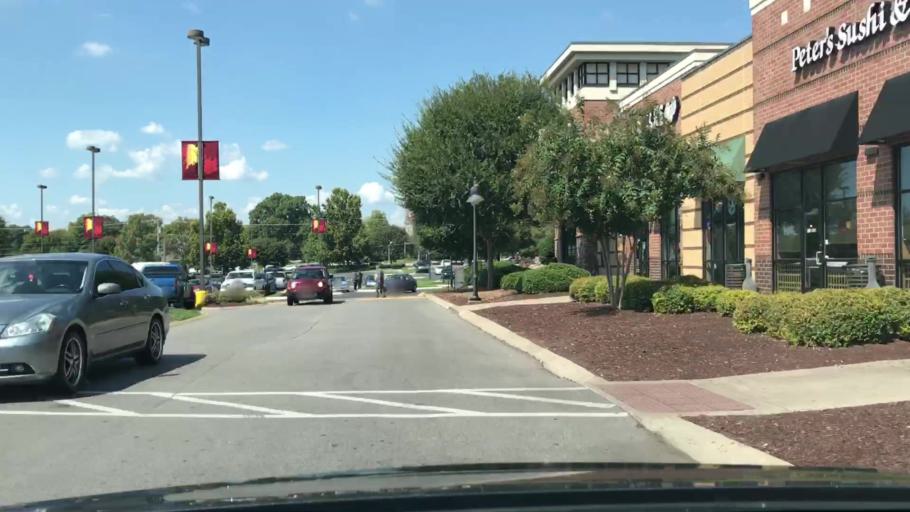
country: US
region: Tennessee
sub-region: Williamson County
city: Brentwood
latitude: 36.0264
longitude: -86.7898
